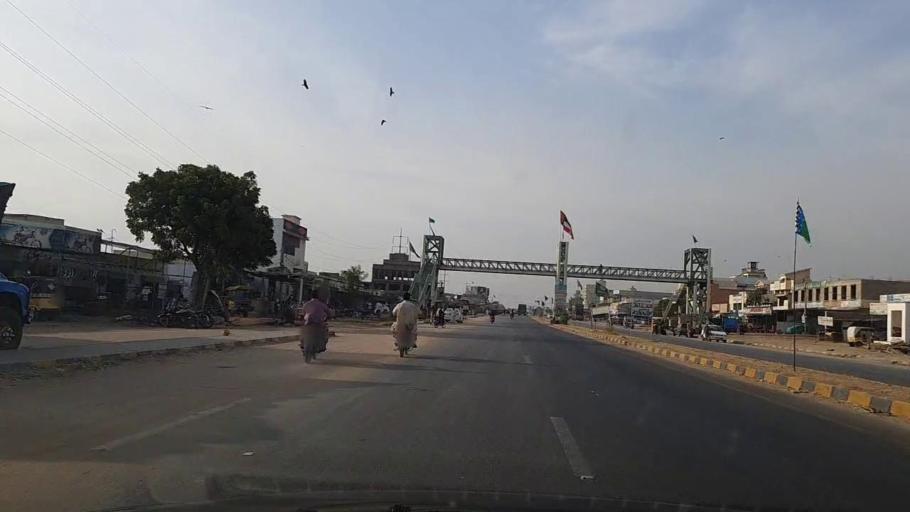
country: PK
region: Sindh
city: Gharo
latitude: 24.7891
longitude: 67.5272
